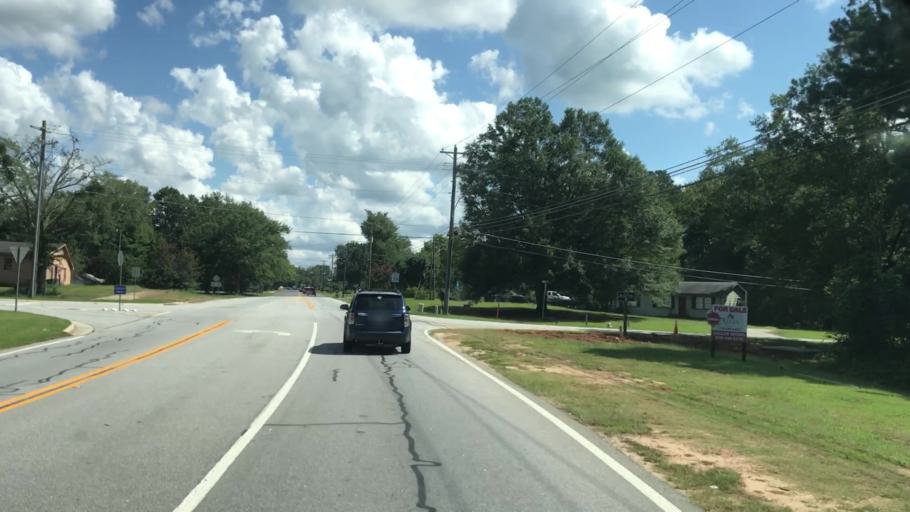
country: US
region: Georgia
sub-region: Walton County
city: Walnut Grove
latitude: 33.7473
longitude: -83.8536
